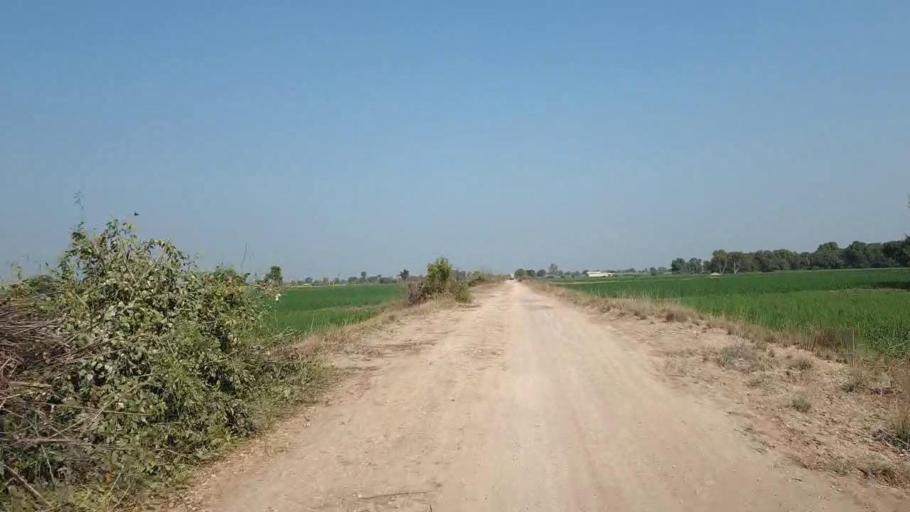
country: PK
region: Sindh
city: Hala
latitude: 25.9170
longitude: 68.4197
